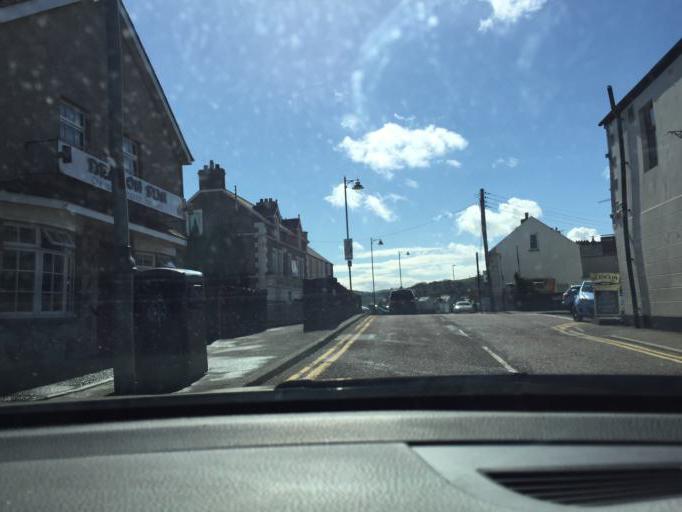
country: GB
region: Northern Ireland
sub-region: Larne District
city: Carnlough
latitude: 54.9920
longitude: -5.9904
